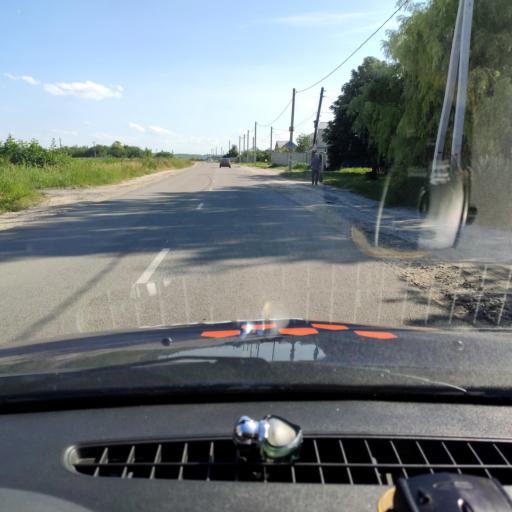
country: RU
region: Voronezj
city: Devitsa
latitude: 51.6349
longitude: 38.9294
